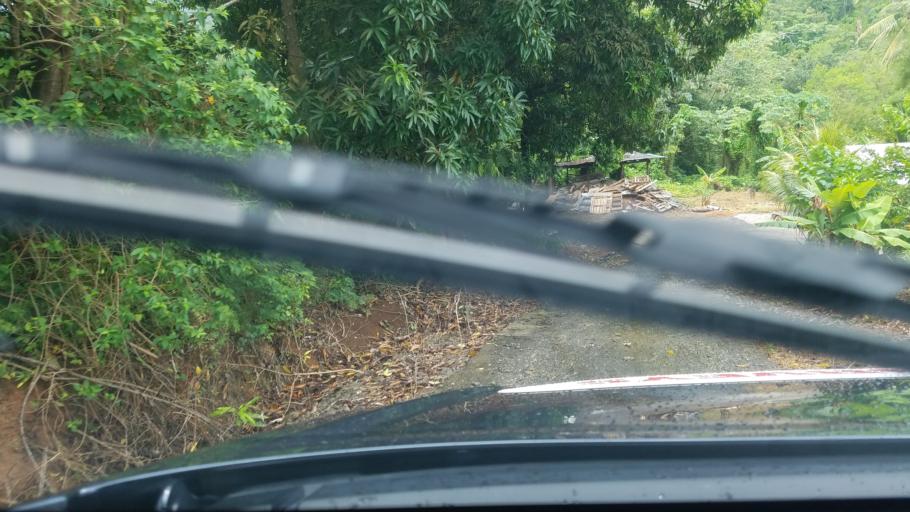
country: LC
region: Castries Quarter
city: Bisee
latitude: 13.9991
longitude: -60.9558
